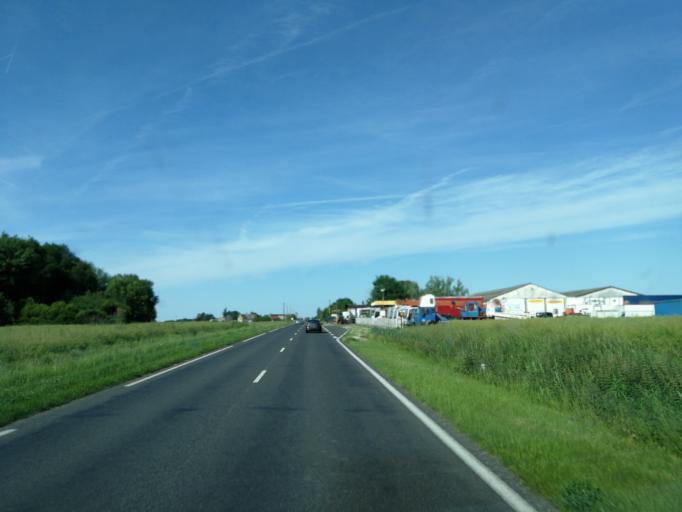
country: FR
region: Centre
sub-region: Departement d'Indre-et-Loire
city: Monnaie
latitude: 47.5291
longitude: 0.8345
